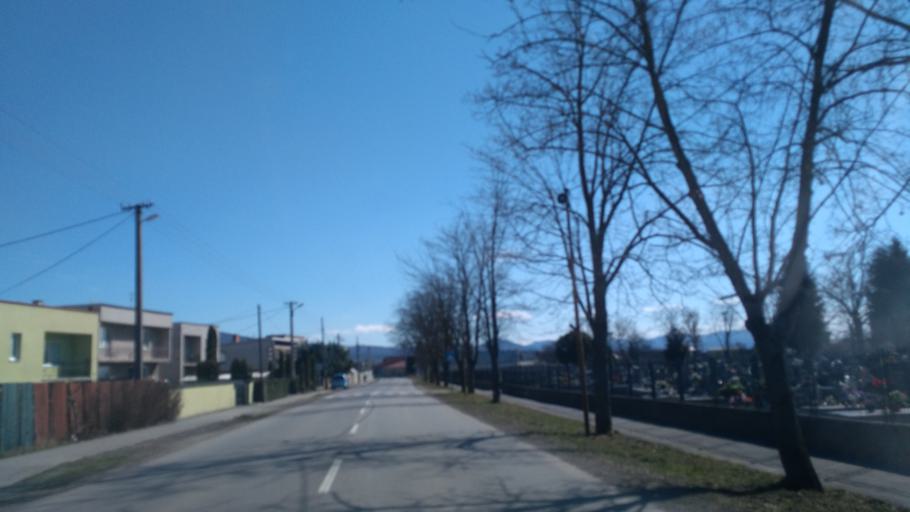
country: SK
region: Kosicky
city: Kosice
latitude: 48.6103
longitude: 21.3204
